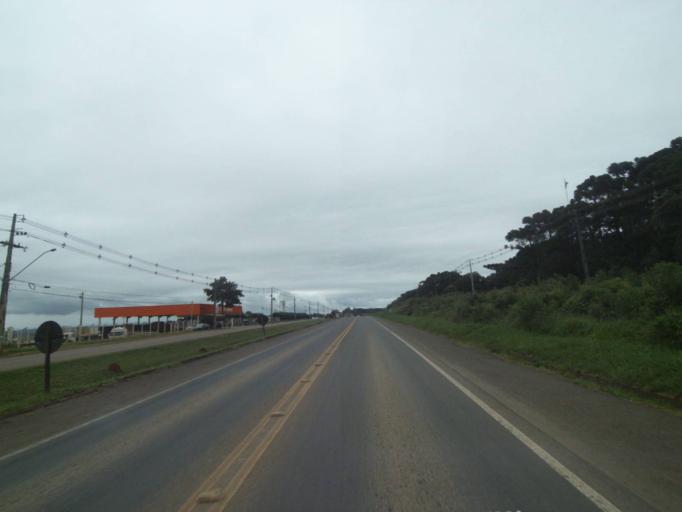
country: BR
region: Parana
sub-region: Telemaco Borba
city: Telemaco Borba
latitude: -24.3775
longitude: -50.6672
